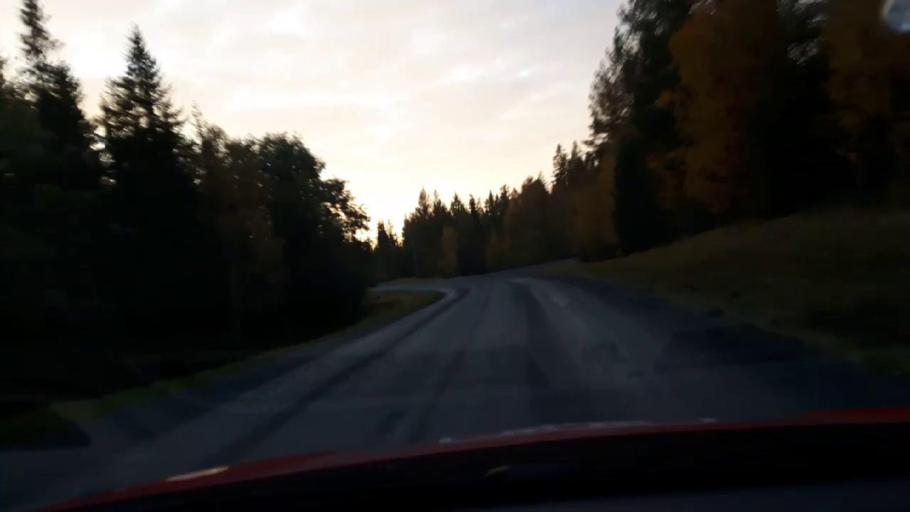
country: SE
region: Jaemtland
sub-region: OEstersunds Kommun
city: Lit
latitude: 63.2839
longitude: 14.7188
